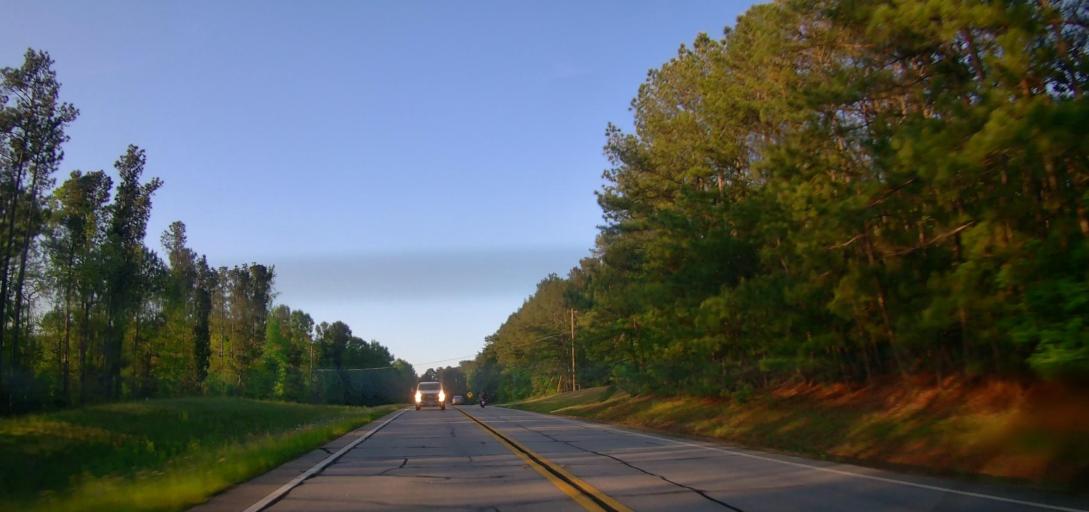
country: US
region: Georgia
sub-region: Newton County
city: Oakwood
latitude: 33.4971
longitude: -83.9513
